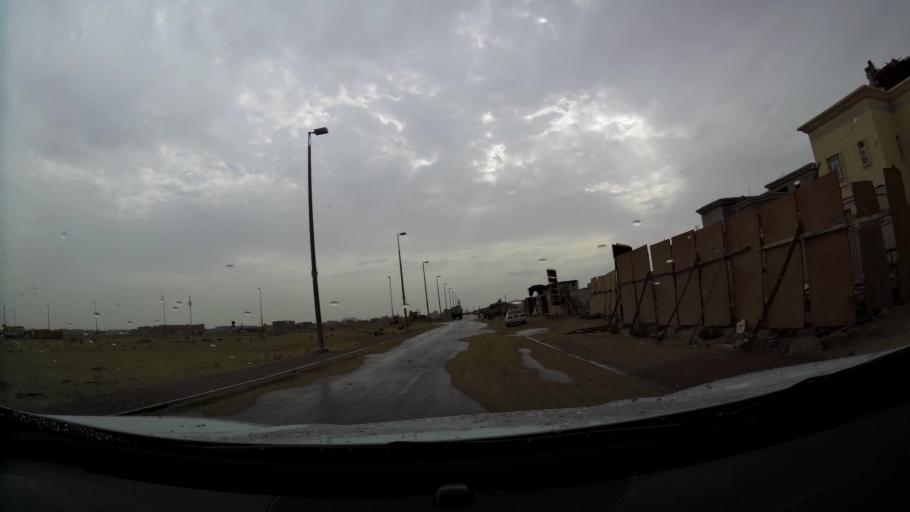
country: AE
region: Abu Dhabi
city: Abu Dhabi
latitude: 24.3692
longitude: 54.6331
